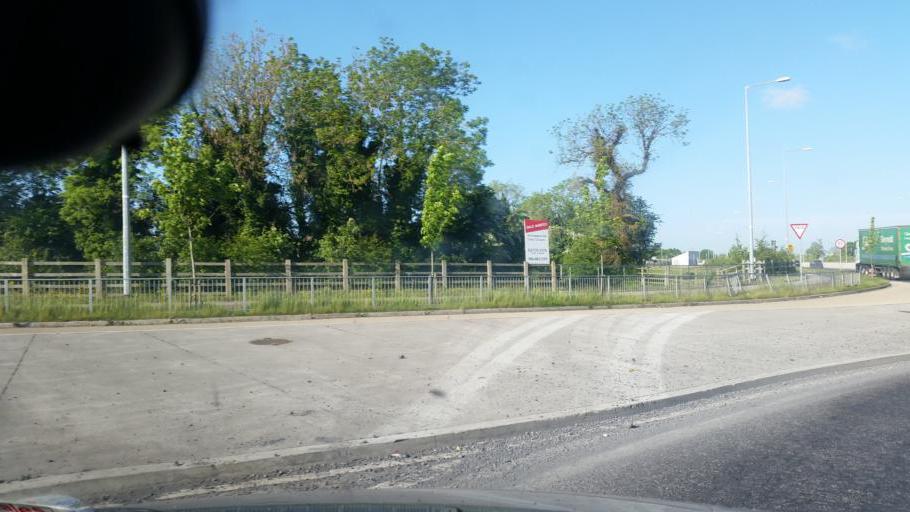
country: IE
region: Leinster
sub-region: Fingal County
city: Blanchardstown
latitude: 53.4286
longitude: -6.3520
